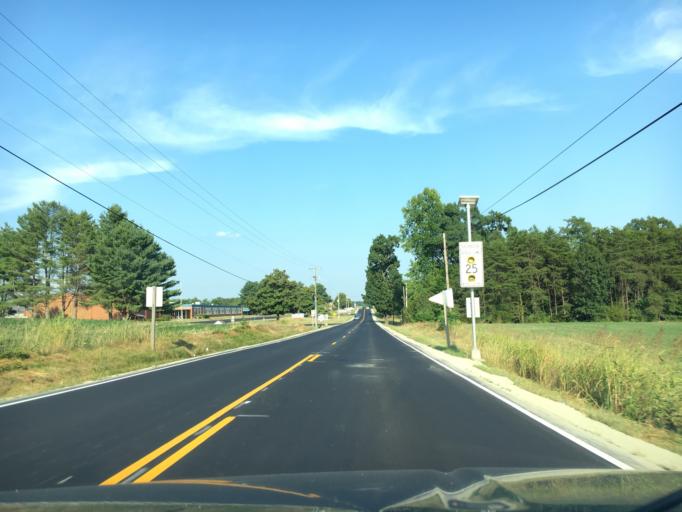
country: US
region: Virginia
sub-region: Franklin County
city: Union Hall
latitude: 36.9872
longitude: -79.7513
